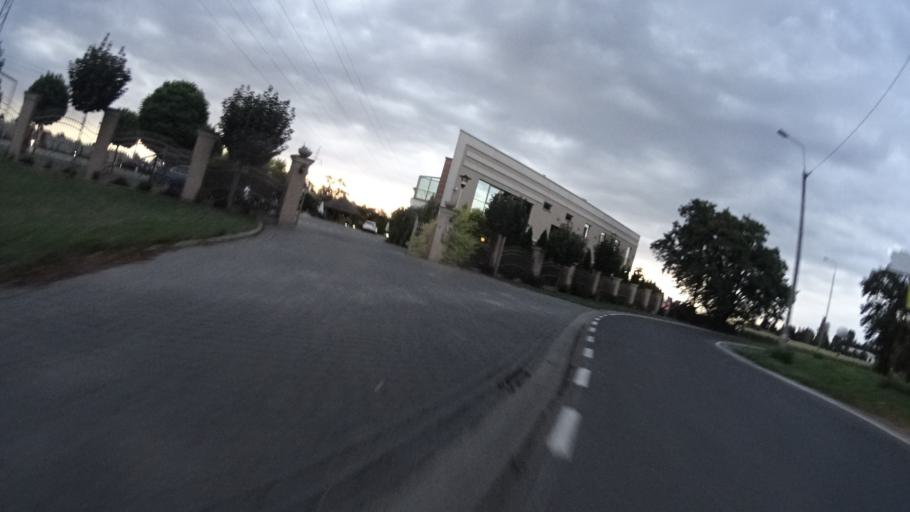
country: PL
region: Masovian Voivodeship
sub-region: Powiat warszawski zachodni
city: Babice
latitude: 52.2280
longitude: 20.8601
